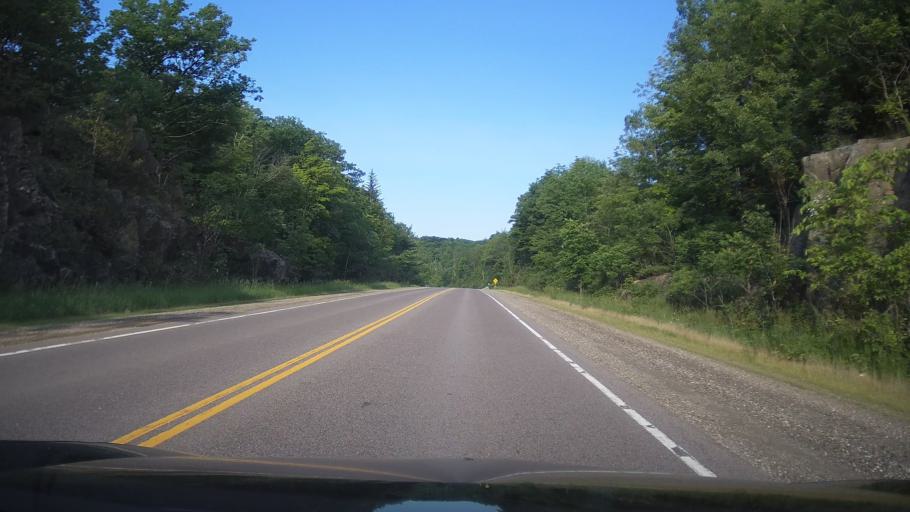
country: CA
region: Ontario
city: Perth
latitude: 44.7854
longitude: -76.7155
